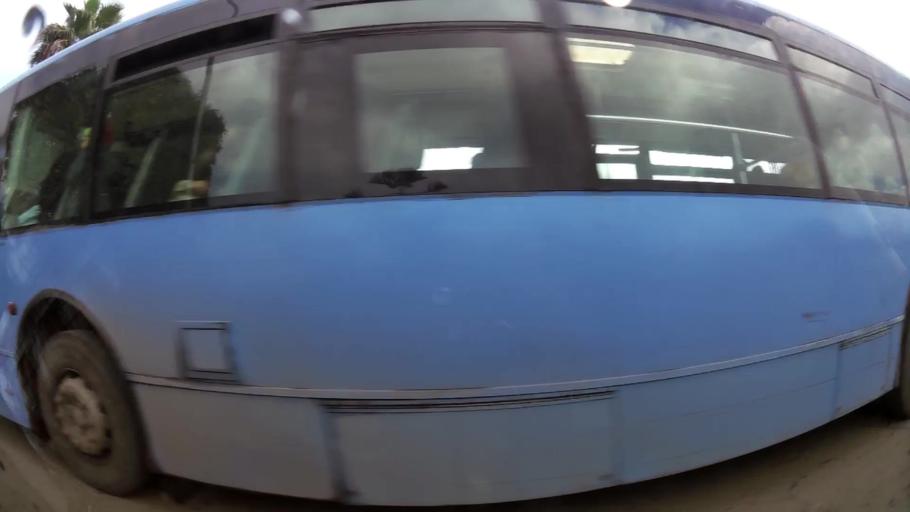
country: MA
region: Grand Casablanca
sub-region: Casablanca
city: Casablanca
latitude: 33.5405
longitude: -7.6394
